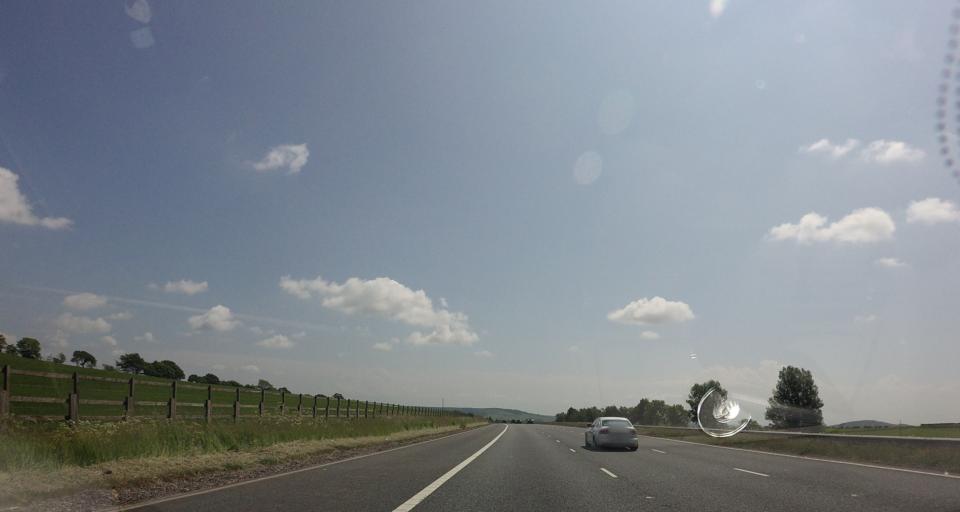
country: GB
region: Scotland
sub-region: Dumfries and Galloway
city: Lockerbie
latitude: 55.0771
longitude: -3.3097
